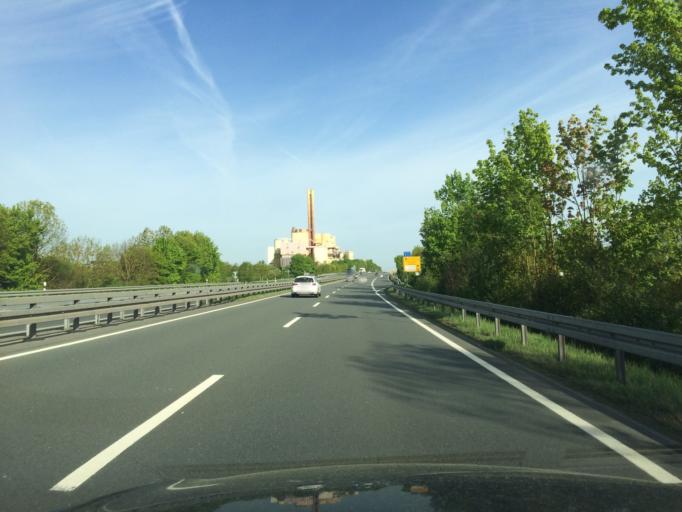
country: DE
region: Bavaria
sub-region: Regierungsbezirk Unterfranken
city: Gerbrunn
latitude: 49.7894
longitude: 10.0014
